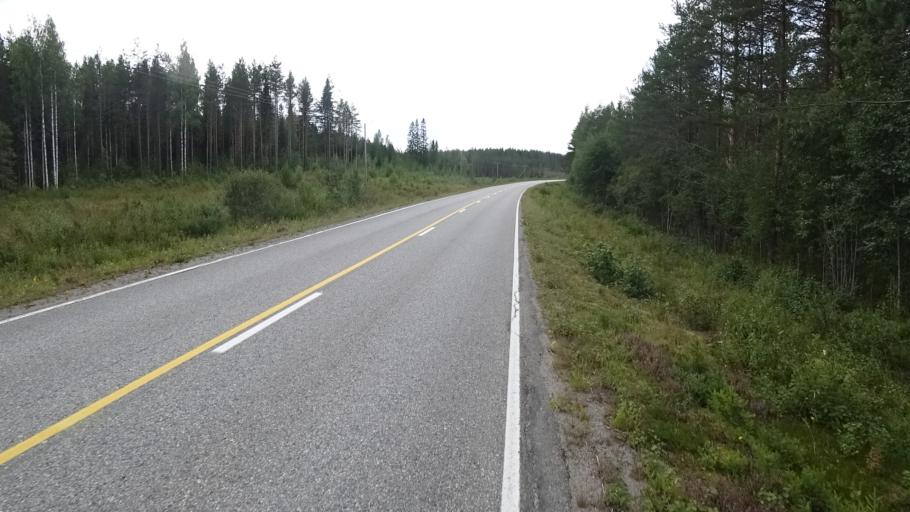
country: FI
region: North Karelia
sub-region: Joensuu
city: Ilomantsi
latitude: 62.6232
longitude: 31.2385
